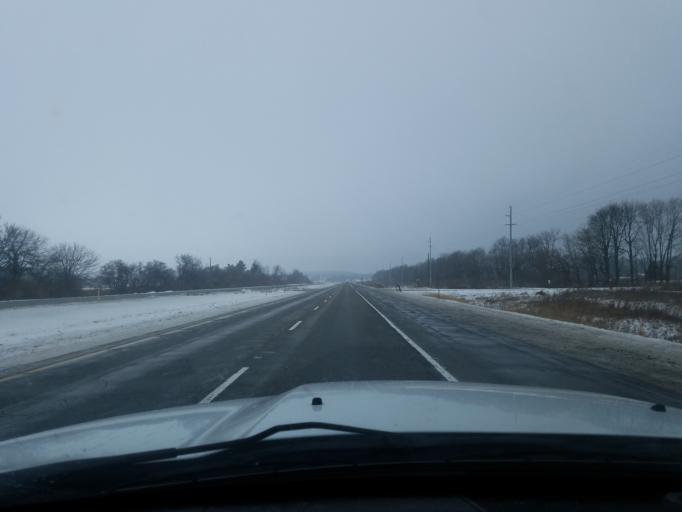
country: US
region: Indiana
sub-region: Fulton County
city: Rochester
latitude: 41.0241
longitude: -86.1782
